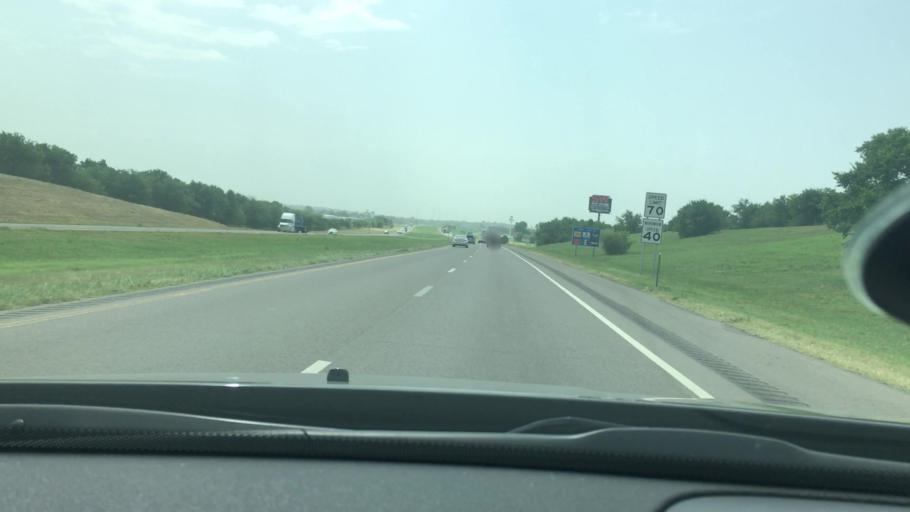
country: US
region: Oklahoma
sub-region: Garvin County
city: Pauls Valley
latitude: 34.7528
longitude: -97.2770
